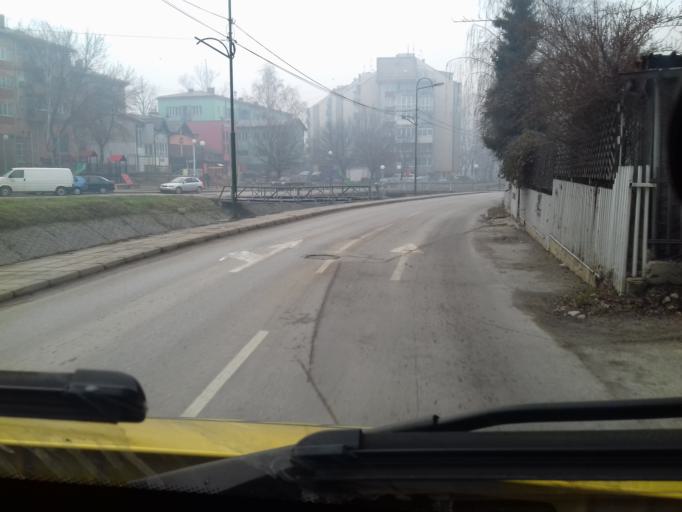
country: BA
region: Federation of Bosnia and Herzegovina
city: Kakanj
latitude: 44.1257
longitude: 18.1150
